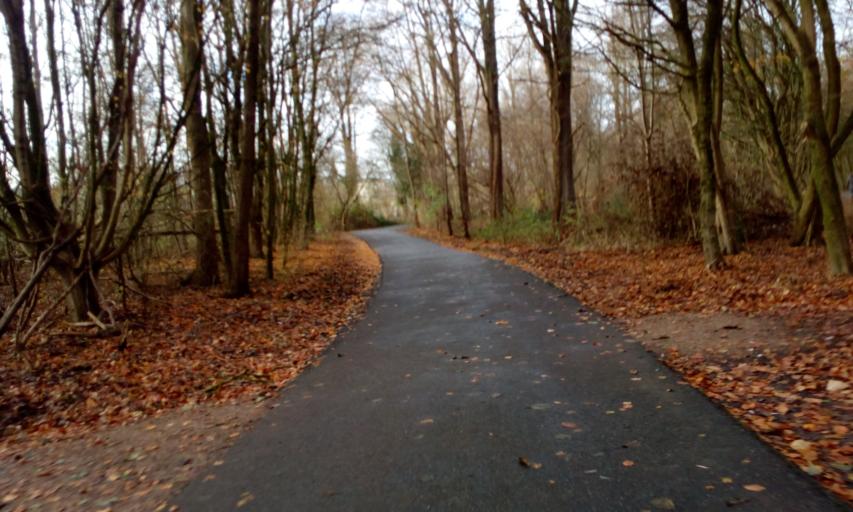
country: NL
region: South Holland
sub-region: Gemeente Lansingerland
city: Bergschenhoek
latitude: 51.9692
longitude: 4.5021
